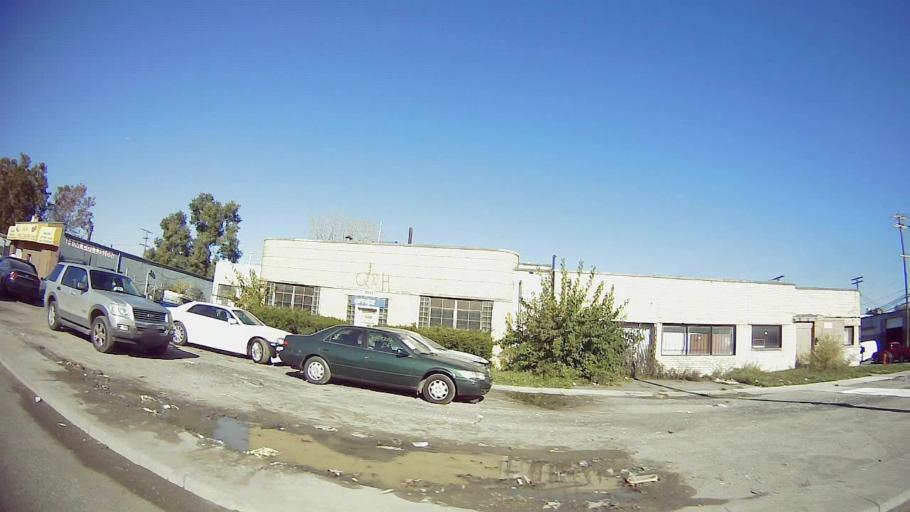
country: US
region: Michigan
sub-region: Wayne County
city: Dearborn
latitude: 42.3585
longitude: -83.1852
